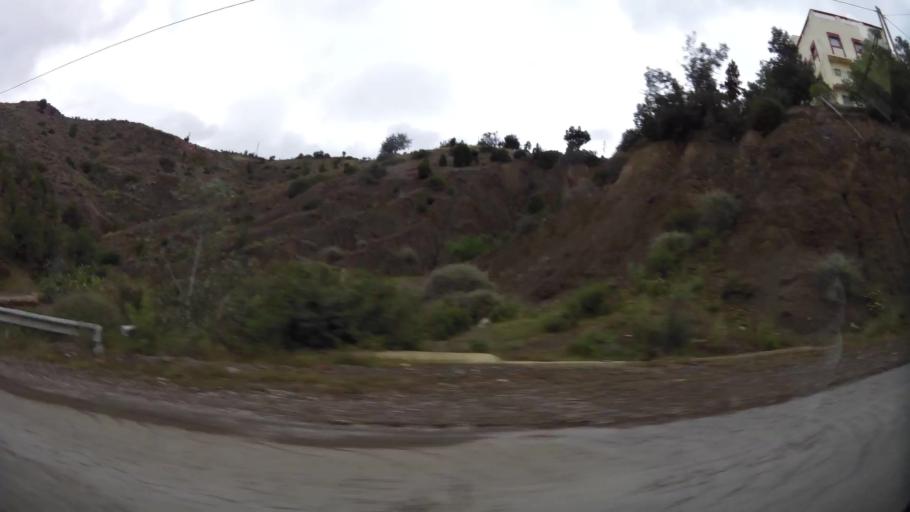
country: MA
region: Taza-Al Hoceima-Taounate
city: Imzourene
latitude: 34.9549
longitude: -3.8088
